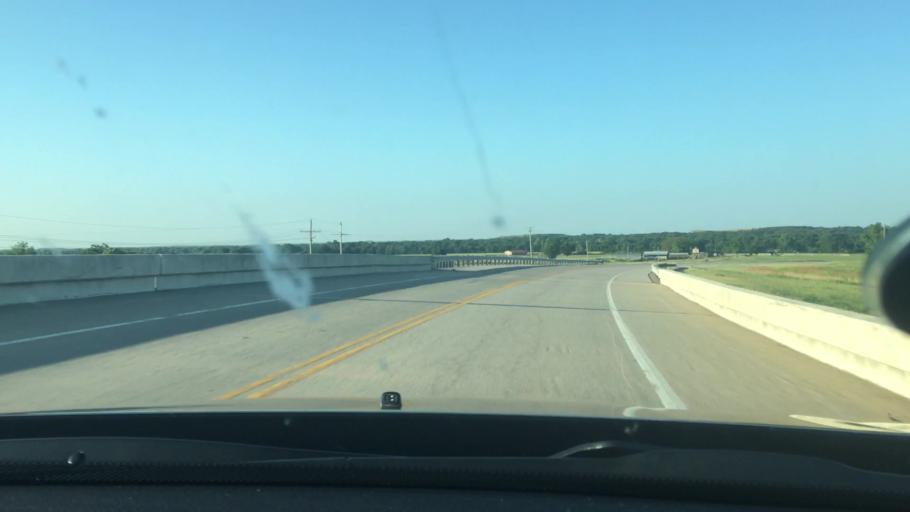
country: US
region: Oklahoma
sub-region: Pontotoc County
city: Ada
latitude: 34.6528
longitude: -96.7954
